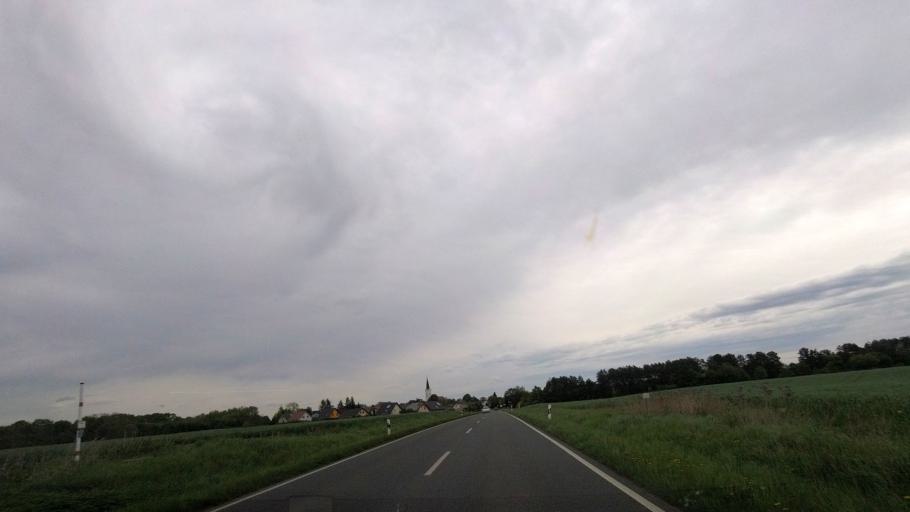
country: DE
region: Brandenburg
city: Lubbenau
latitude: 51.8580
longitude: 13.9248
